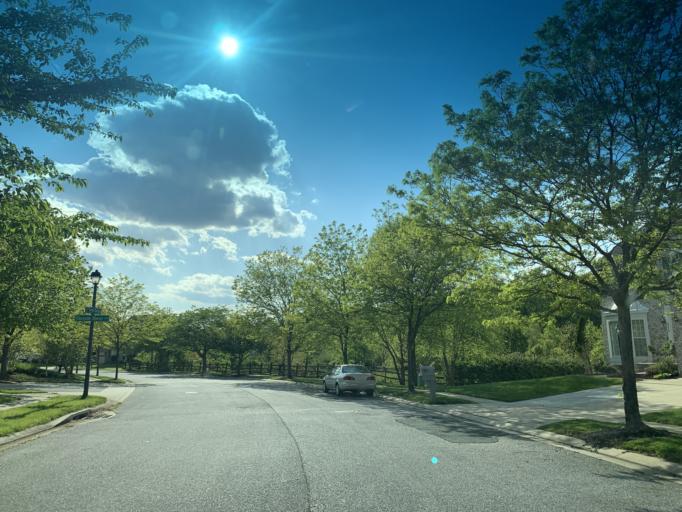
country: US
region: Maryland
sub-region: Baltimore County
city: White Marsh
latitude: 39.4081
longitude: -76.4299
